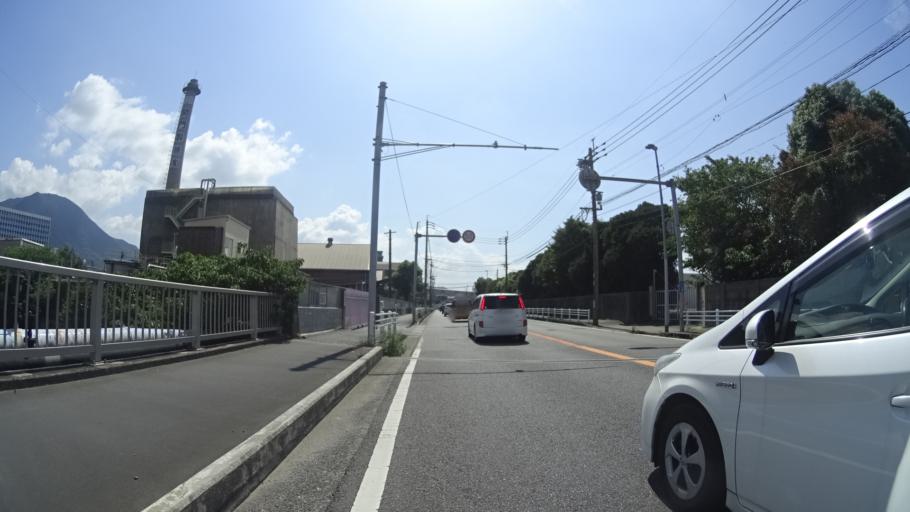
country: JP
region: Yamaguchi
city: Shimonoseki
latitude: 33.9151
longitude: 130.9377
